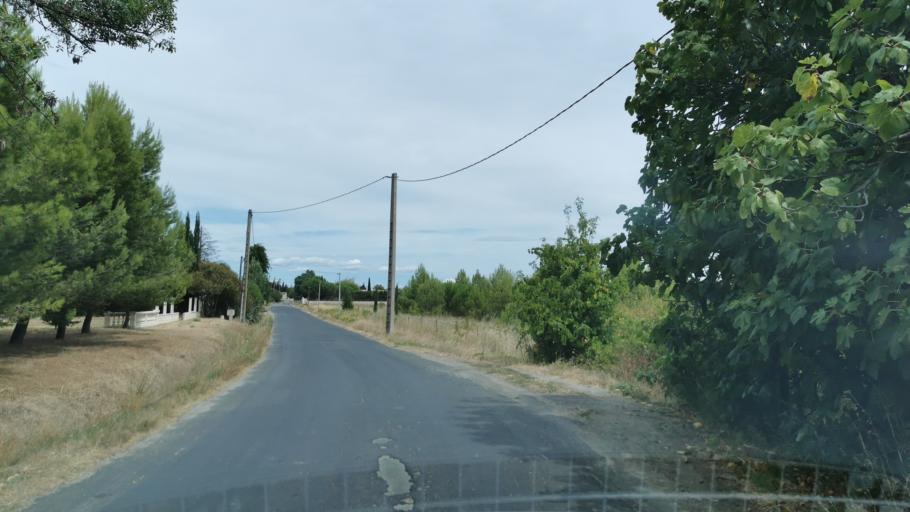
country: FR
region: Languedoc-Roussillon
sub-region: Departement de l'Aude
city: Ginestas
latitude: 43.2717
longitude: 2.8816
